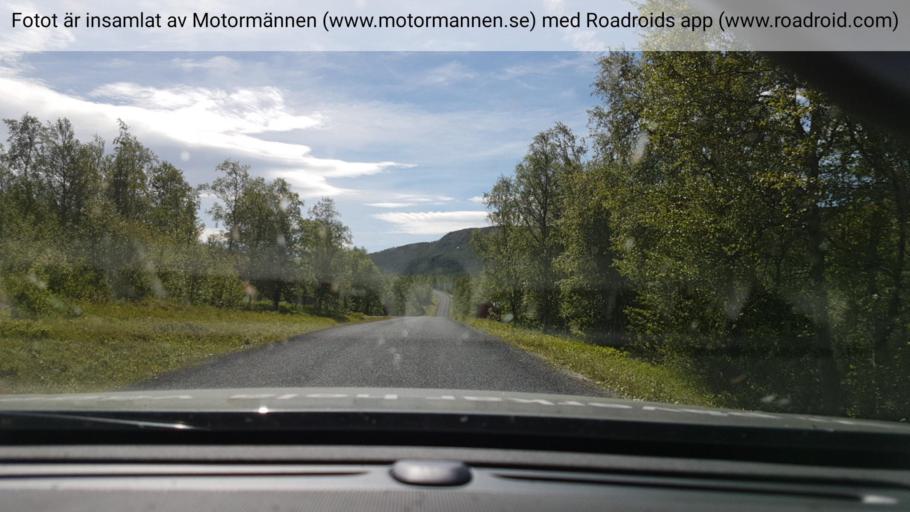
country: SE
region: Vaesterbotten
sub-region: Vilhelmina Kommun
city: Sjoberg
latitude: 65.2901
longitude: 15.2934
